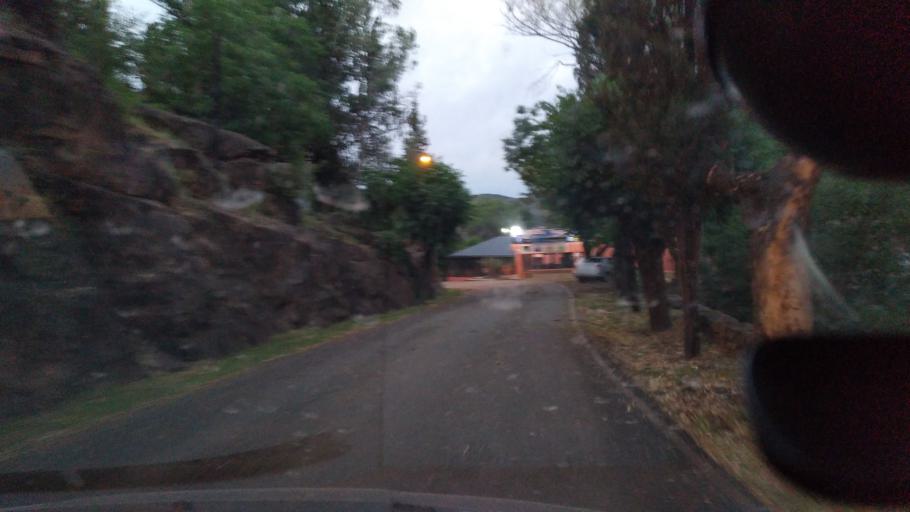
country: AR
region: Cordoba
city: Villa Las Rosas
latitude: -31.8720
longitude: -65.0325
